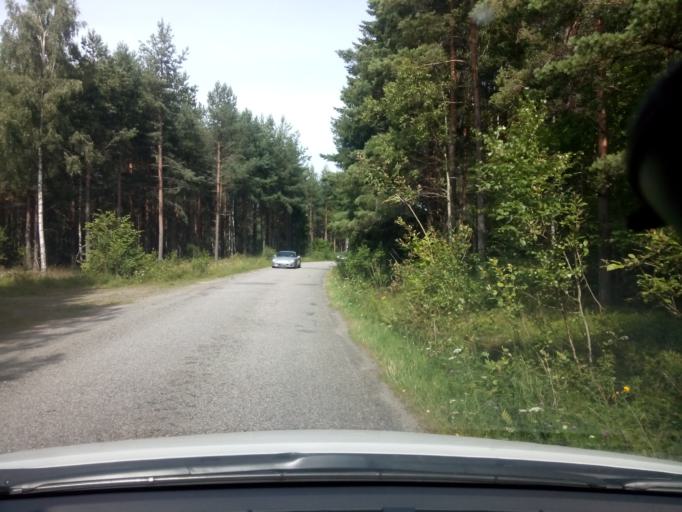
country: SE
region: Soedermanland
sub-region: Trosa Kommun
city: Trosa
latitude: 58.7628
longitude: 17.3714
